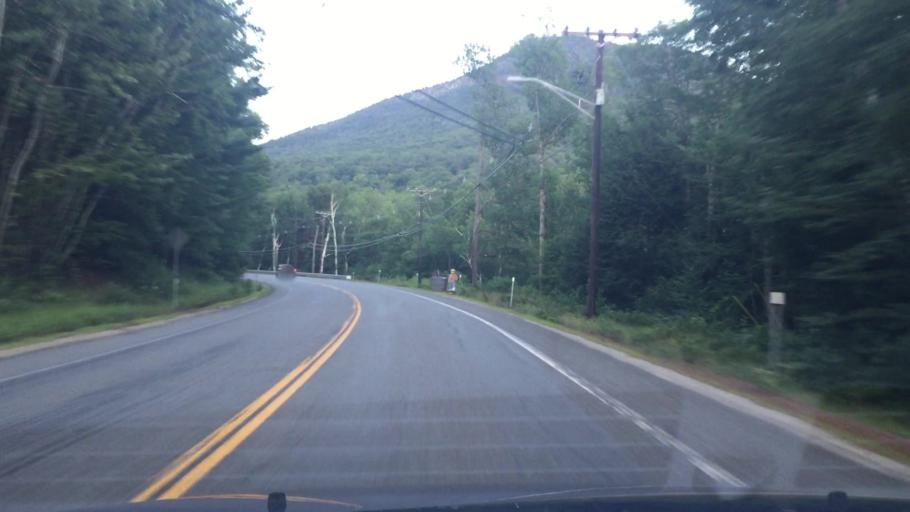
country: US
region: New Hampshire
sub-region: Grafton County
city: Woodstock
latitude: 44.0579
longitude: -71.6305
